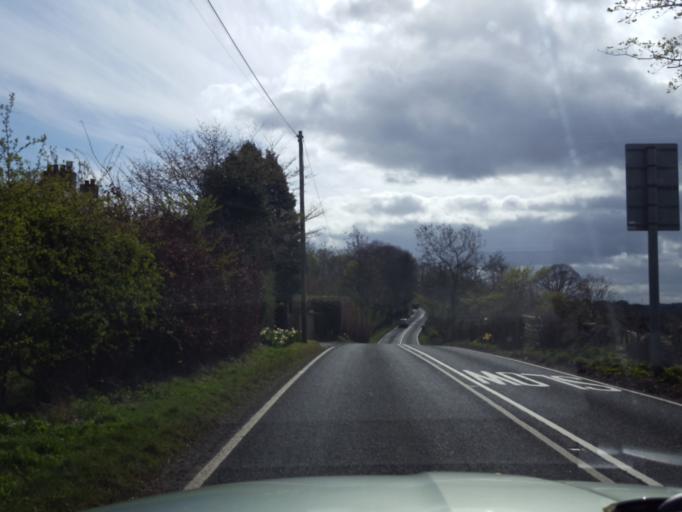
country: GB
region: Scotland
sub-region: West Lothian
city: Linlithgow
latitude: 55.9609
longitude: -3.6451
